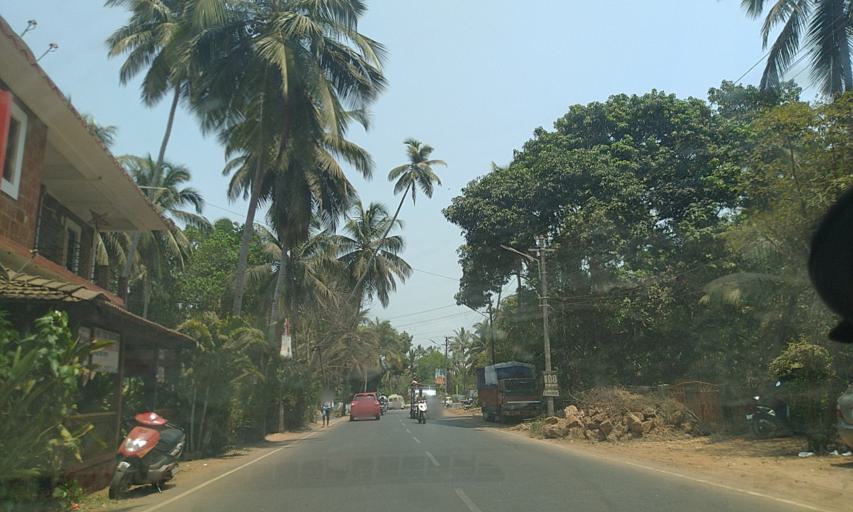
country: IN
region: Goa
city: Calangute
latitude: 15.5477
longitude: 73.7684
